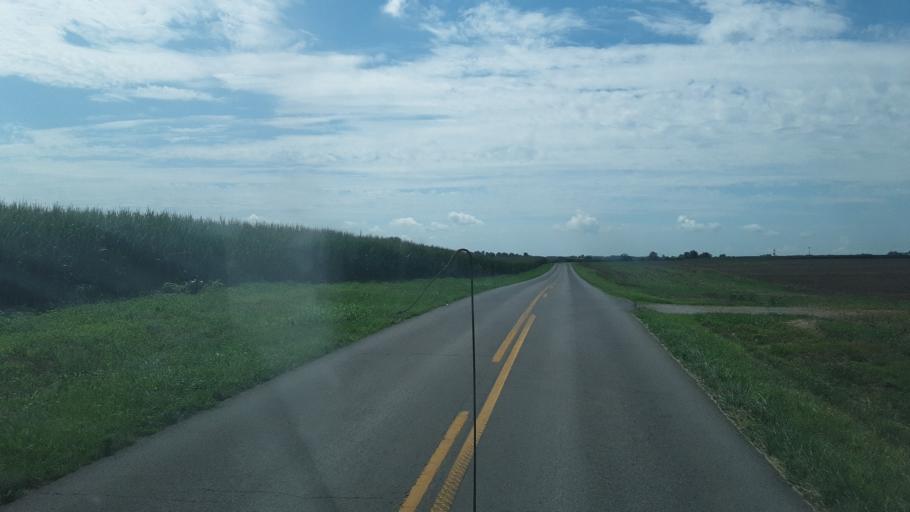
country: US
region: Kentucky
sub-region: Christian County
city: Oak Grove
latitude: 36.7484
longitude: -87.3180
